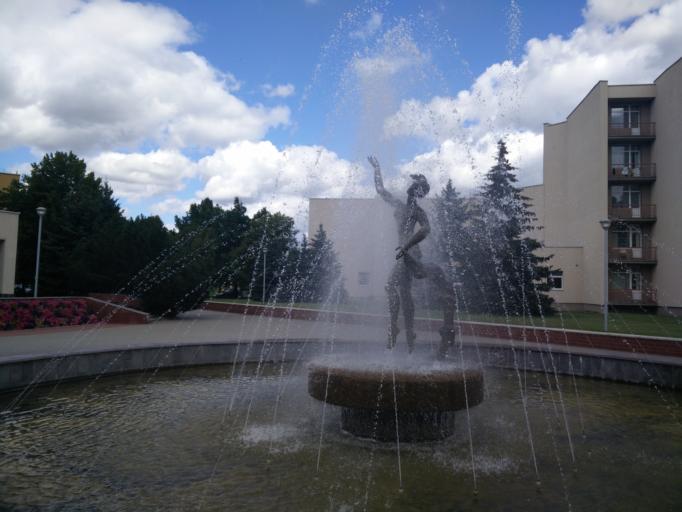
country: LT
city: Birstonas
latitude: 54.6014
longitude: 24.0297
